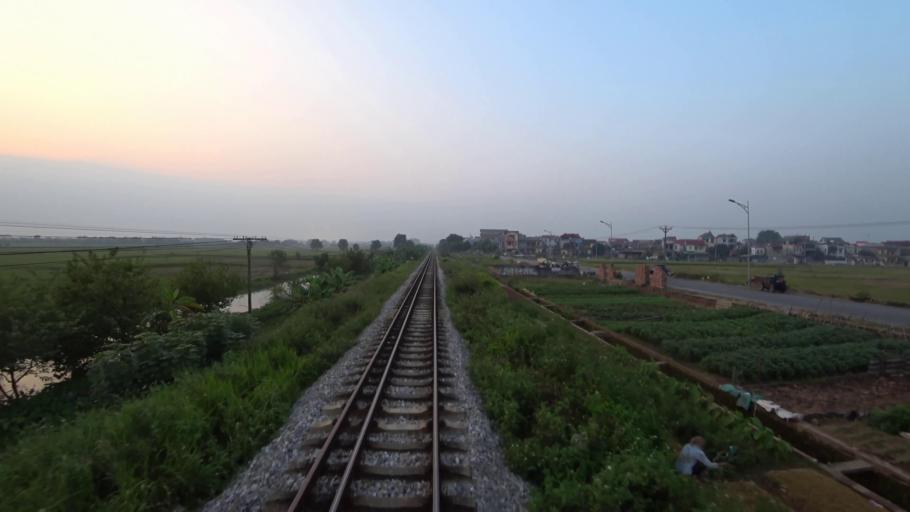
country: VN
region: Ha Noi
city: Dong Anh
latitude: 21.1275
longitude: 105.8790
